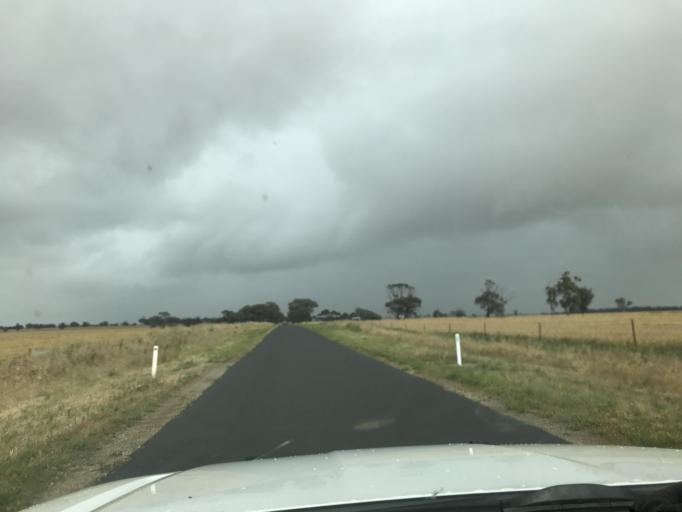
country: AU
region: South Australia
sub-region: Tatiara
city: Bordertown
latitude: -36.3442
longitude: 141.2303
